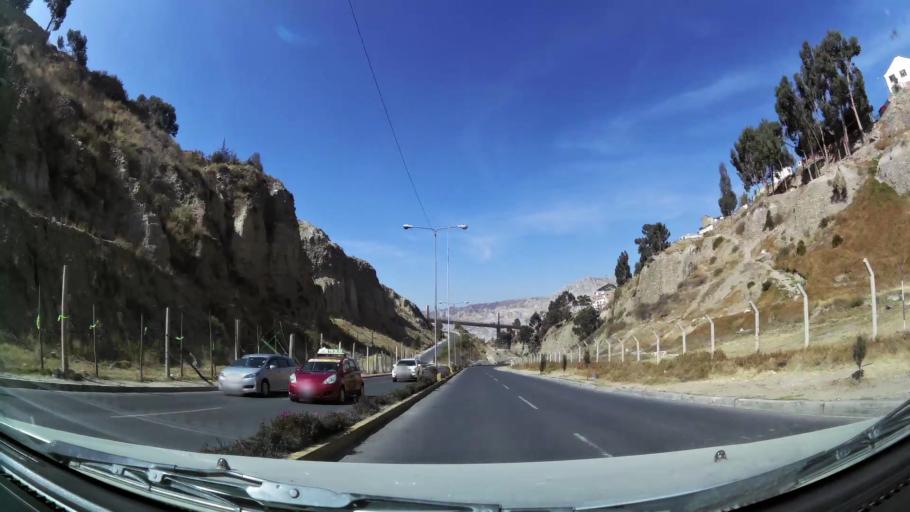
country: BO
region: La Paz
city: La Paz
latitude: -16.5104
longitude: -68.1159
